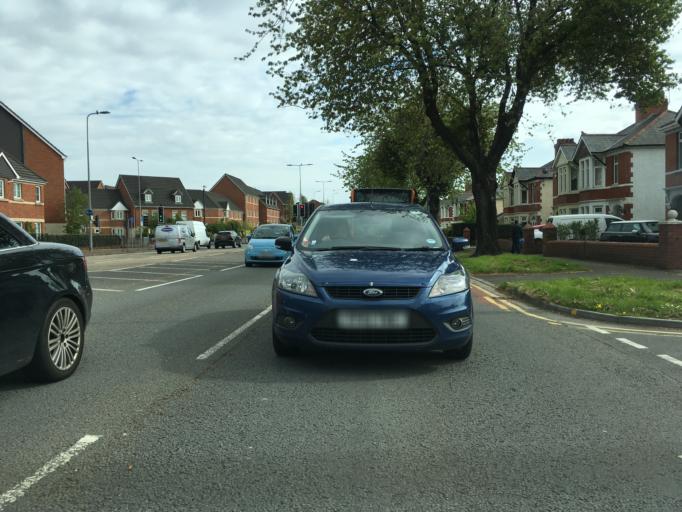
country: GB
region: Wales
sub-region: Cardiff
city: Cardiff
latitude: 51.5235
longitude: -3.2023
